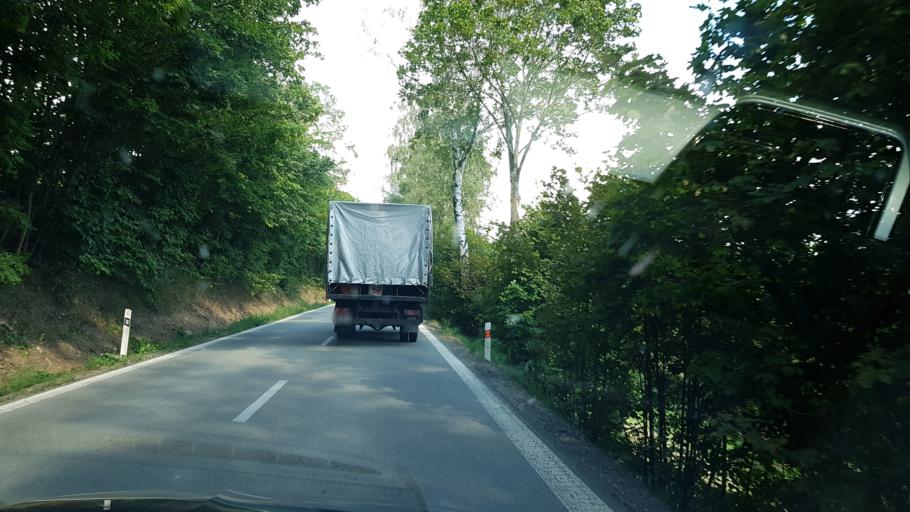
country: CZ
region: Pardubicky
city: Jablonne nad Orlici
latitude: 50.0944
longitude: 16.5751
